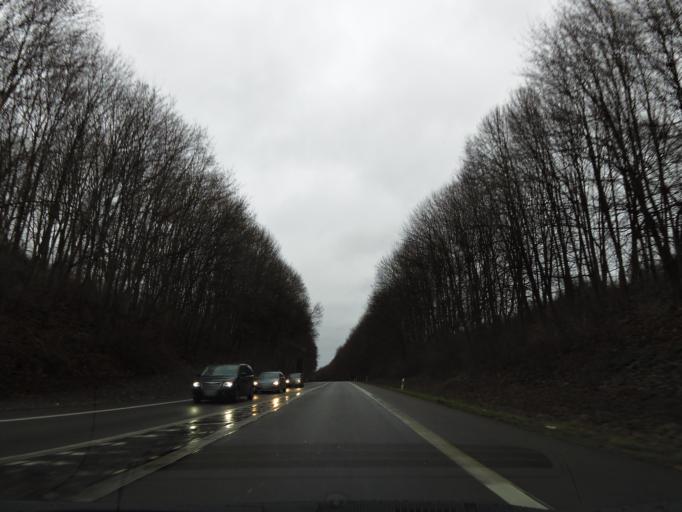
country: DE
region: North Rhine-Westphalia
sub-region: Regierungsbezirk Koln
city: Aachen
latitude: 50.8078
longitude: 6.0752
